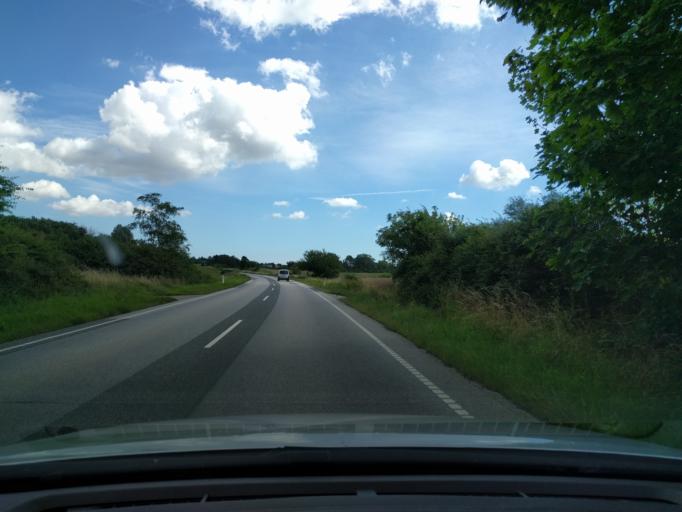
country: DK
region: Zealand
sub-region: Guldborgsund Kommune
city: Stubbekobing
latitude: 54.9220
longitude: 12.0281
